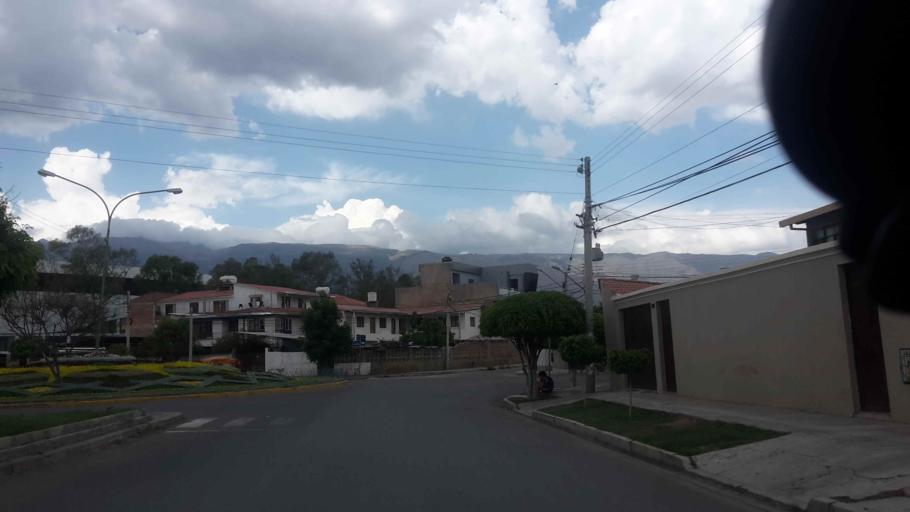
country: BO
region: Cochabamba
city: Cochabamba
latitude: -17.4034
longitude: -66.1742
